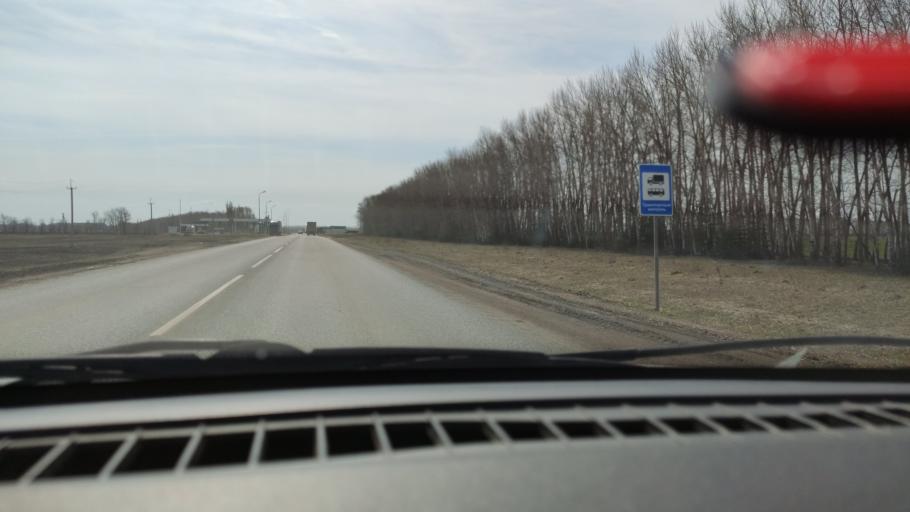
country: RU
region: Bashkortostan
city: Dyurtyuli
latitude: 55.4227
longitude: 54.8080
